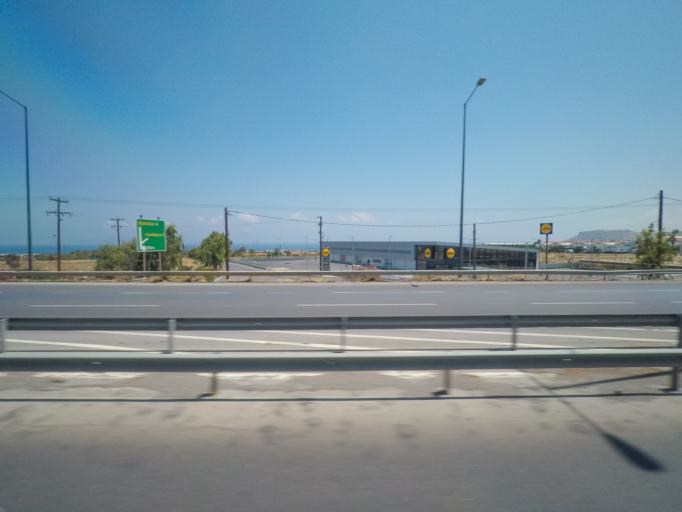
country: GR
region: Crete
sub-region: Nomos Irakleiou
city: Nea Alikarnassos
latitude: 35.3267
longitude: 25.1784
